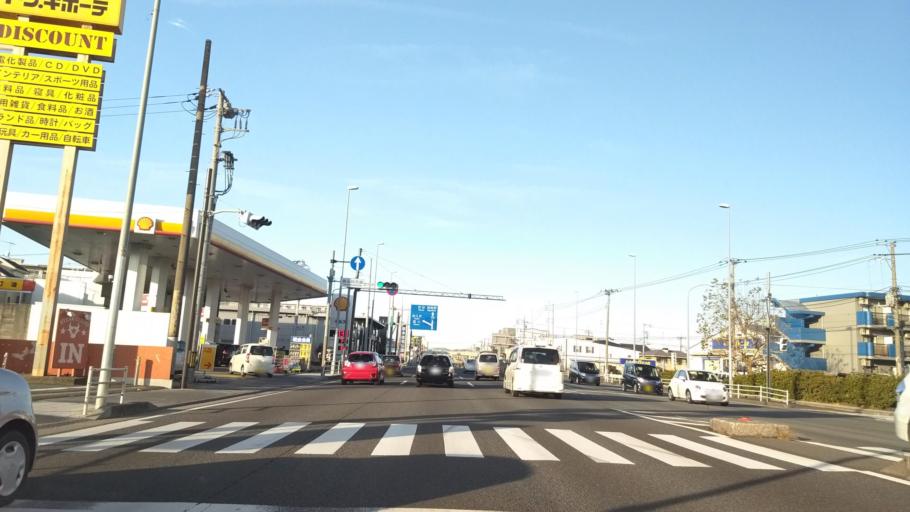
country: JP
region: Kanagawa
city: Atsugi
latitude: 35.4551
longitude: 139.3589
